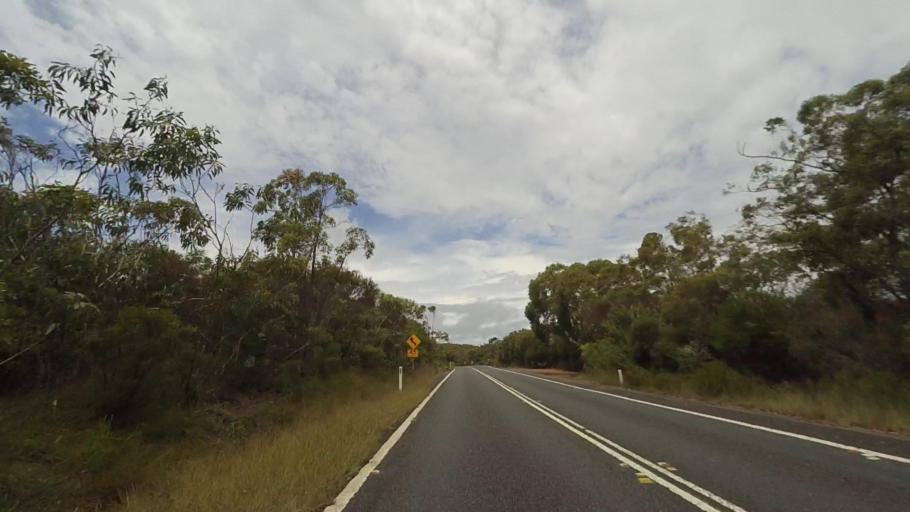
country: AU
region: New South Wales
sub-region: Sutherland Shire
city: Grays Point
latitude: -34.1208
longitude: 151.0756
